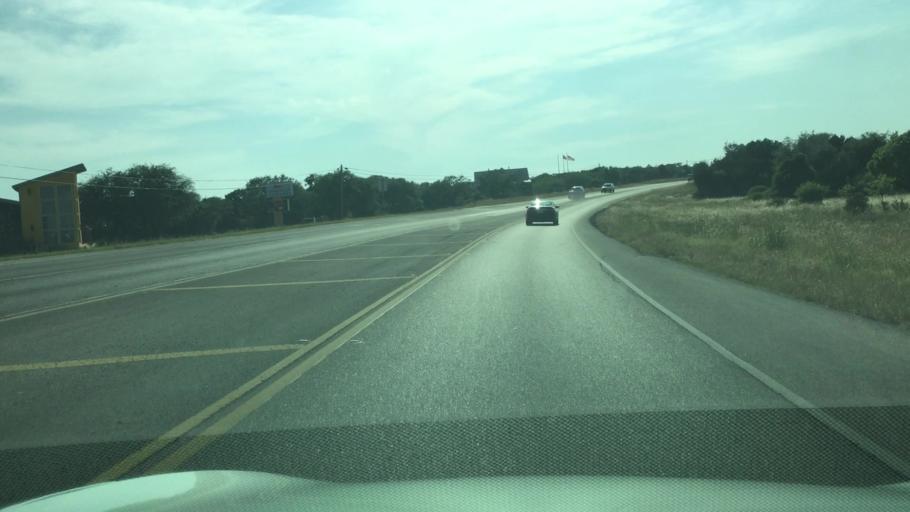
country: US
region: Texas
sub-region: Hays County
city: Wimberley
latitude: 29.9166
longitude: -98.0492
